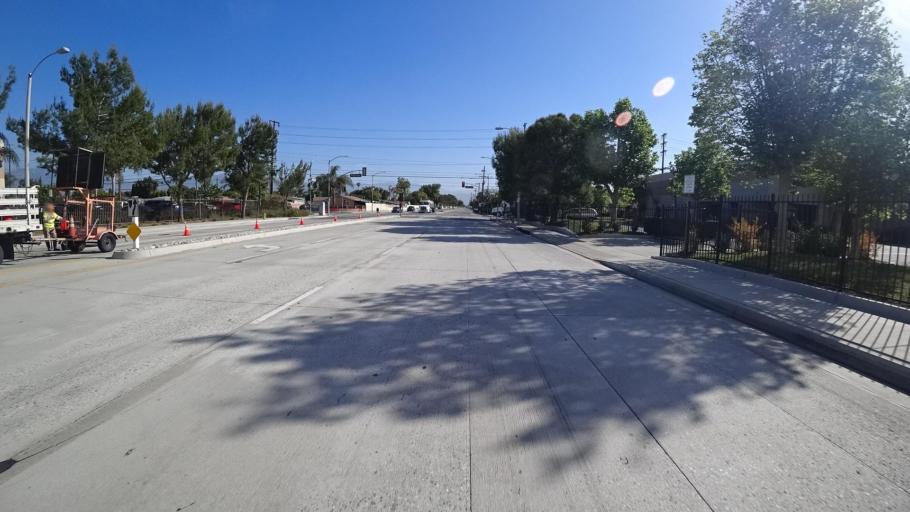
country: US
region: California
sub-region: Los Angeles County
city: Avocado Heights
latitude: 34.0462
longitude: -117.9860
